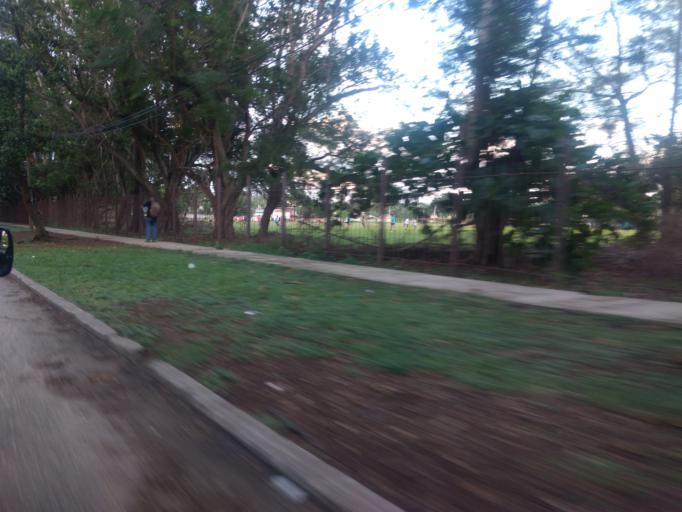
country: CU
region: La Habana
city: Cerro
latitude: 23.0881
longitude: -82.4620
